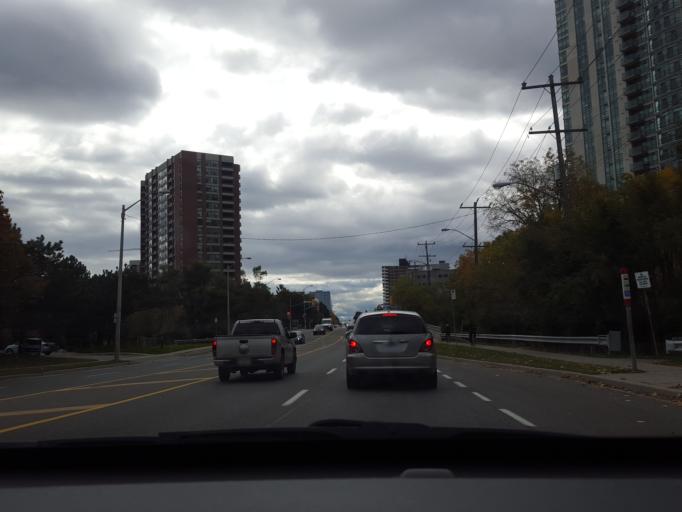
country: CA
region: Ontario
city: Scarborough
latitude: 43.7870
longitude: -79.2902
